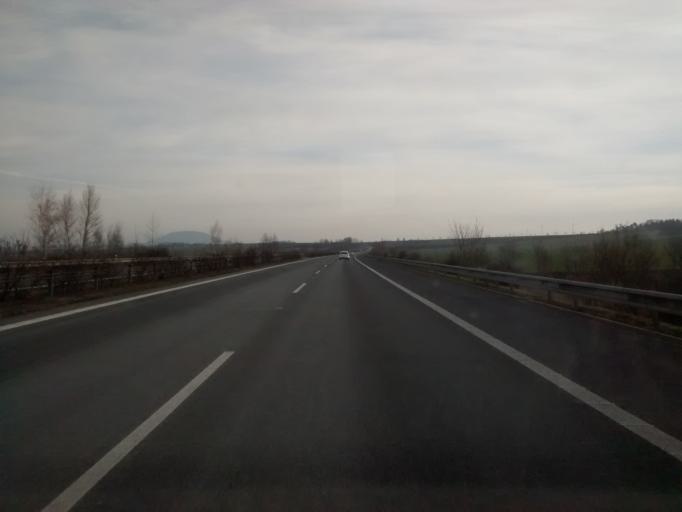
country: CZ
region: Ustecky
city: Roudnice nad Labem
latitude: 50.4271
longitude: 14.1997
